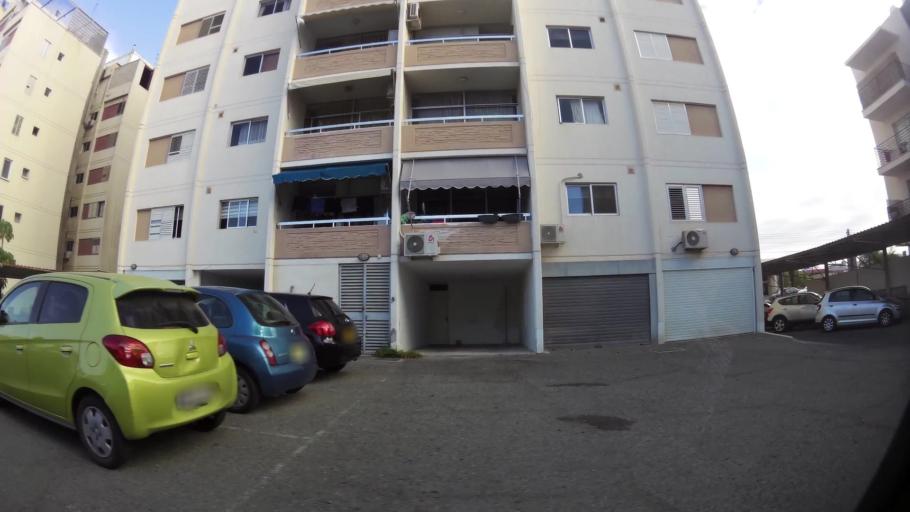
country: CY
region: Lefkosia
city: Nicosia
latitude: 35.1490
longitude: 33.3559
